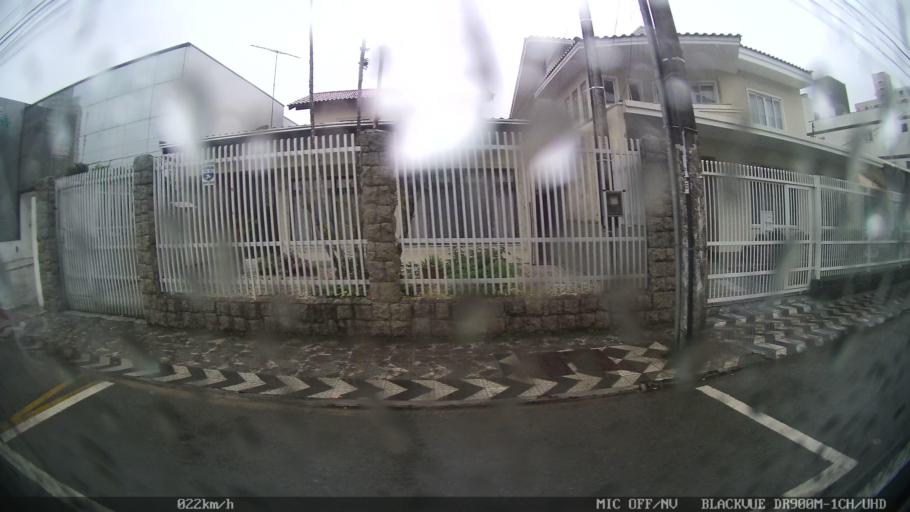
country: BR
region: Santa Catarina
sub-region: Itajai
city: Itajai
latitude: -26.9074
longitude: -48.6654
